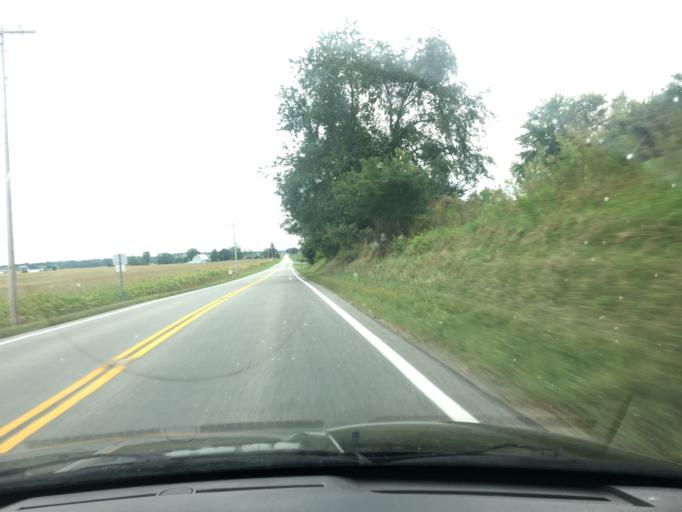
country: US
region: Ohio
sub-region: Champaign County
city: Urbana
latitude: 40.1531
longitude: -83.6828
